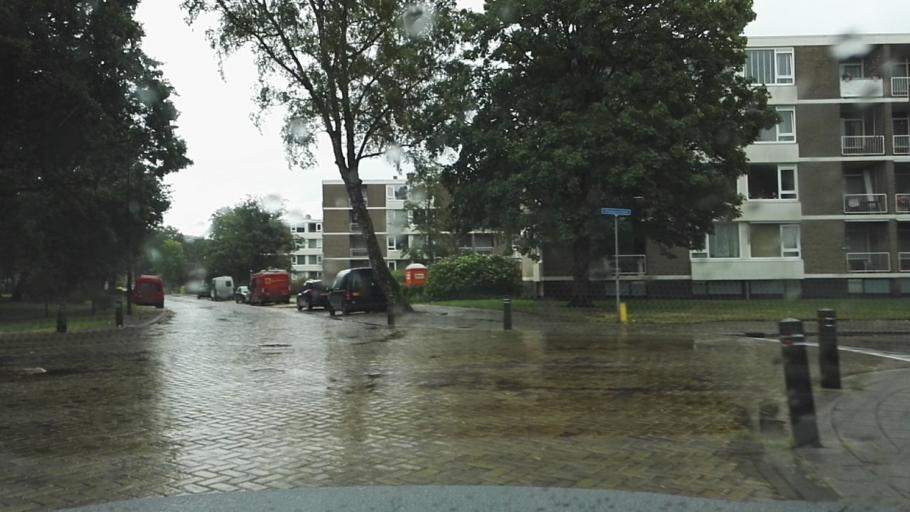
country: NL
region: Gelderland
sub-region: Gemeente Apeldoorn
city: Apeldoorn
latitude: 52.2045
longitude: 5.9337
